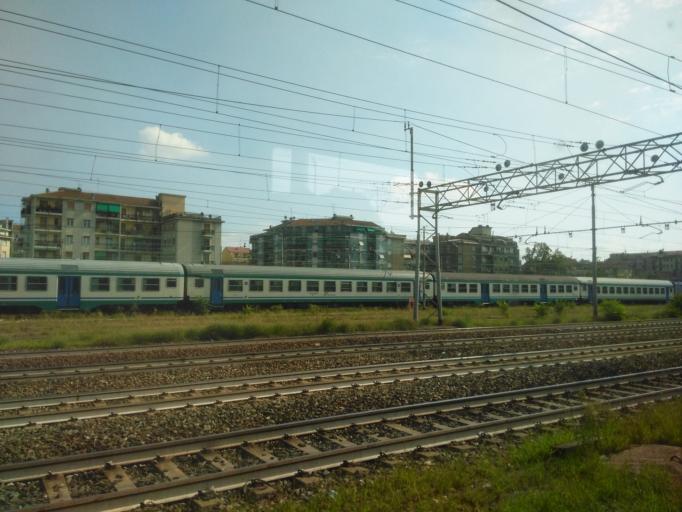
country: IT
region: Lombardy
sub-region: Citta metropolitana di Milano
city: Milano
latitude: 45.4926
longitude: 9.2112
